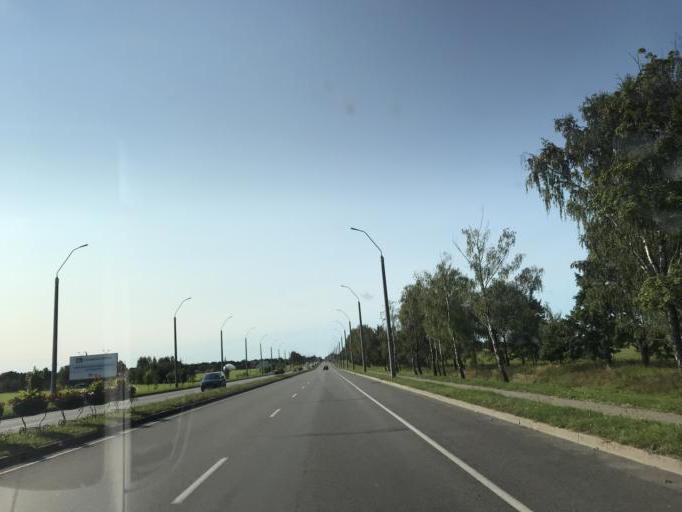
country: BY
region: Mogilev
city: Buynichy
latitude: 53.8720
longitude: 30.2629
